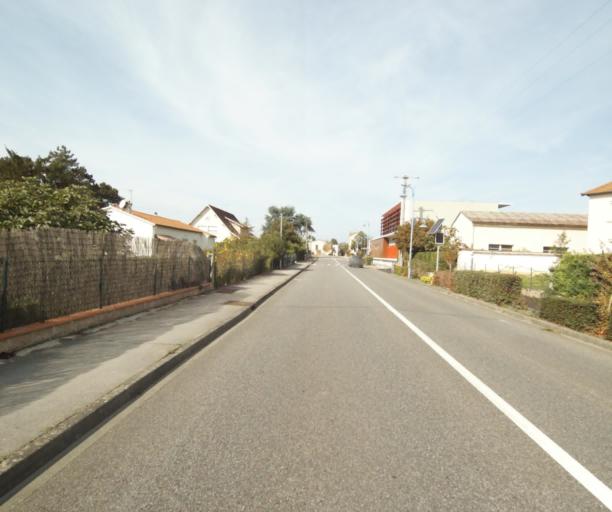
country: FR
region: Midi-Pyrenees
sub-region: Departement du Tarn-et-Garonne
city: Corbarieu
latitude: 43.9433
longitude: 1.3691
